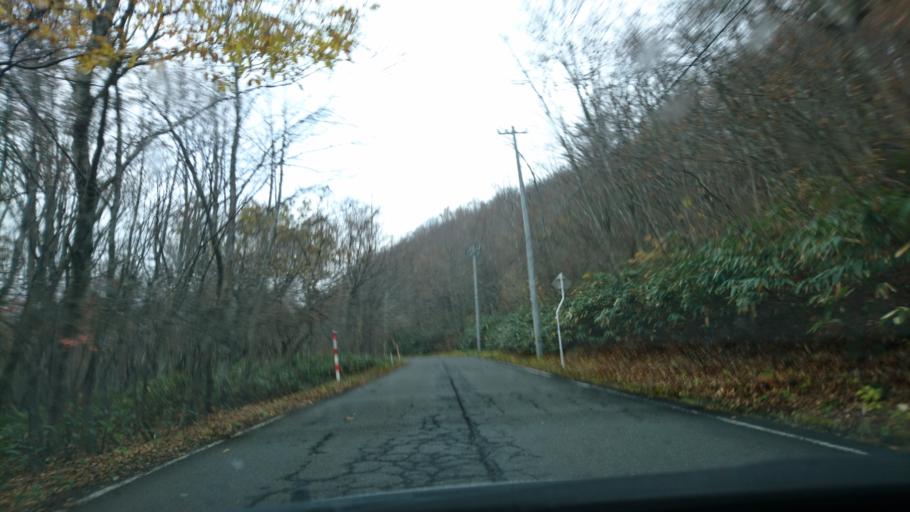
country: JP
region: Iwate
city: Ichinoseki
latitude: 38.9181
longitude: 140.8450
